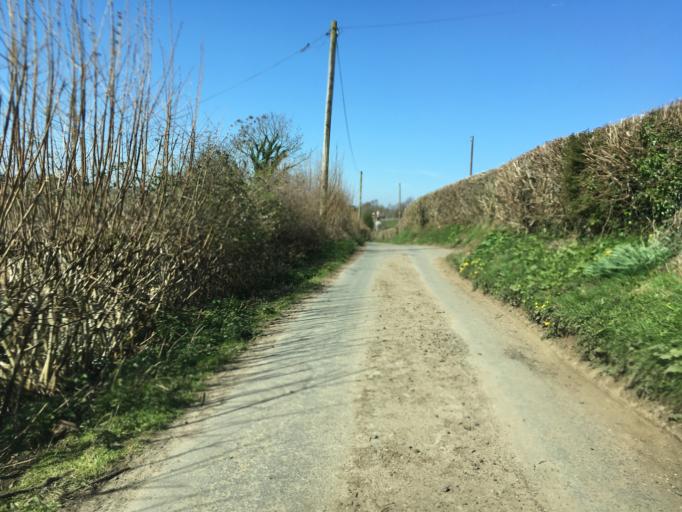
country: GB
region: England
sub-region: Gloucestershire
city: Dursley
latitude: 51.6663
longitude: -2.3591
